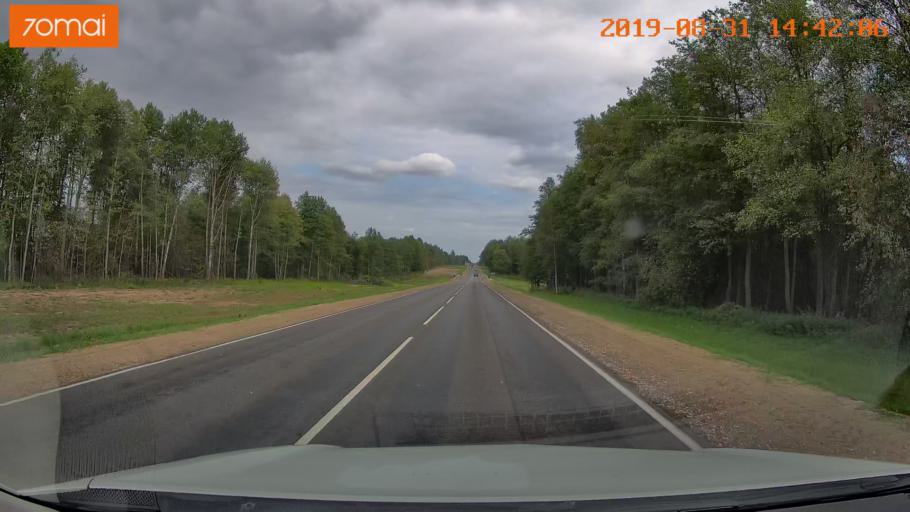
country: RU
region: Smolensk
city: Yekimovichi
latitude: 54.2061
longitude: 33.6015
